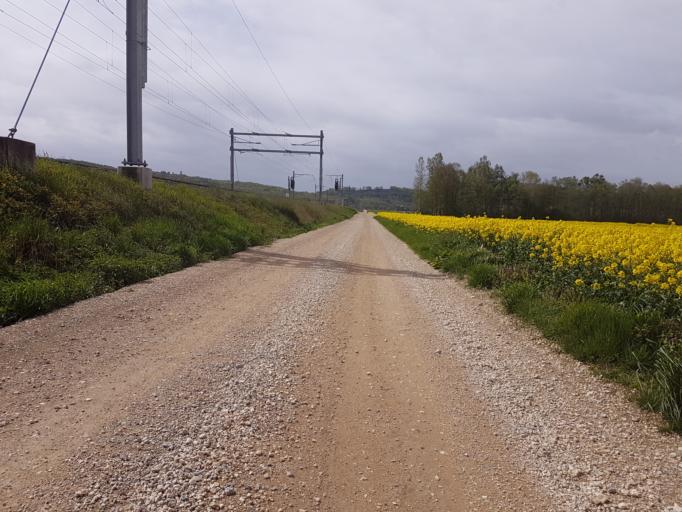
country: CH
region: Vaud
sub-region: Jura-Nord vaudois District
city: Bavois
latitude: 46.6787
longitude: 6.5558
